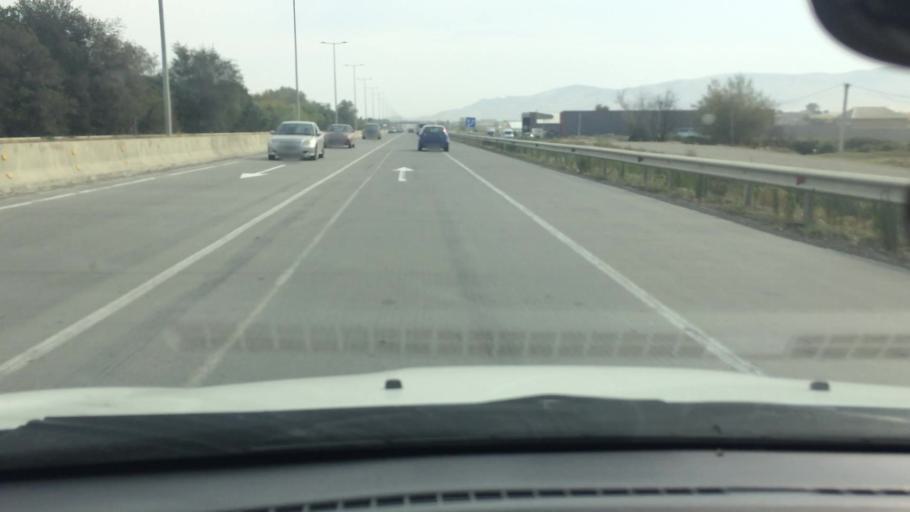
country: GE
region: Kvemo Kartli
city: Rust'avi
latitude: 41.6193
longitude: 44.9281
